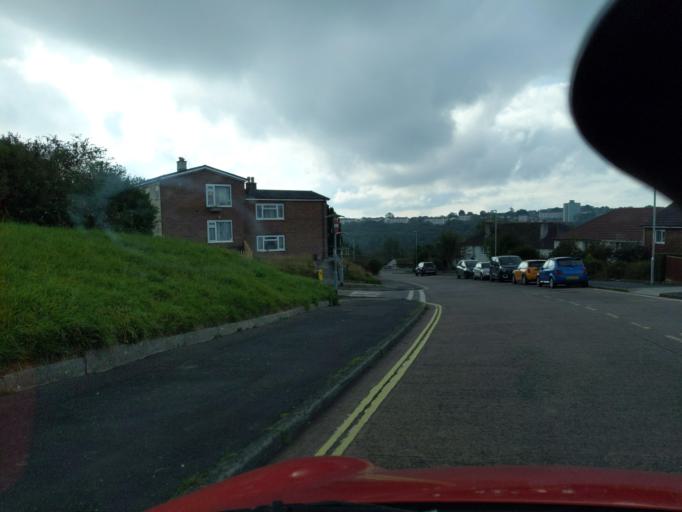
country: GB
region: England
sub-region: Plymouth
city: Plymouth
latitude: 50.4221
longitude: -4.1613
